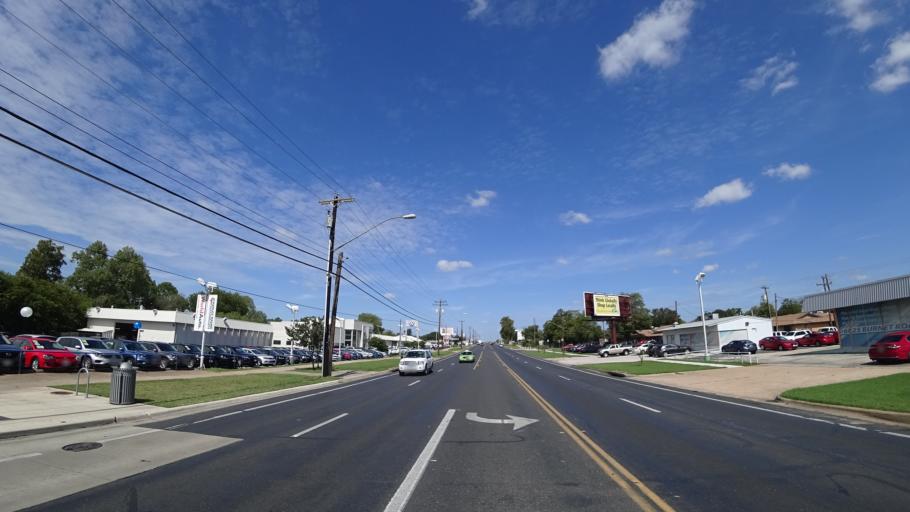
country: US
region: Texas
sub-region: Travis County
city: Austin
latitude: 30.3457
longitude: -97.7373
